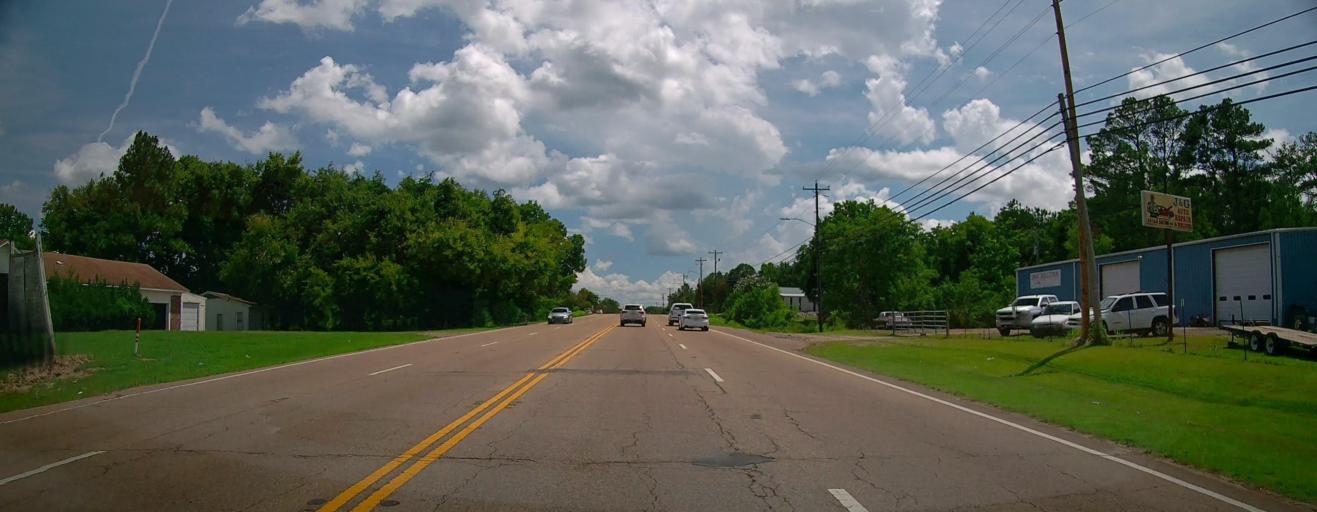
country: US
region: Mississippi
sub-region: Lee County
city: Verona
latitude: 34.1853
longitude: -88.7199
